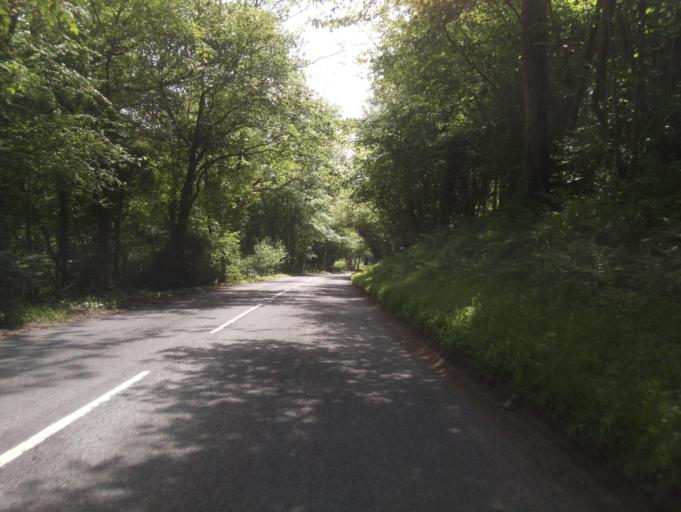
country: GB
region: England
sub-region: Herefordshire
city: Llanrothal
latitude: 51.8846
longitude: -2.7754
